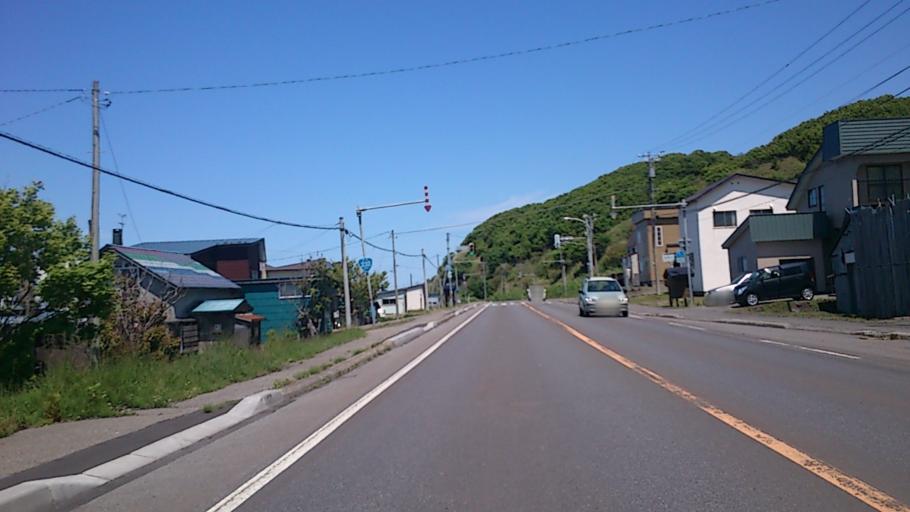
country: JP
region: Hokkaido
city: Rumoi
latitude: 43.9687
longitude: 141.6465
